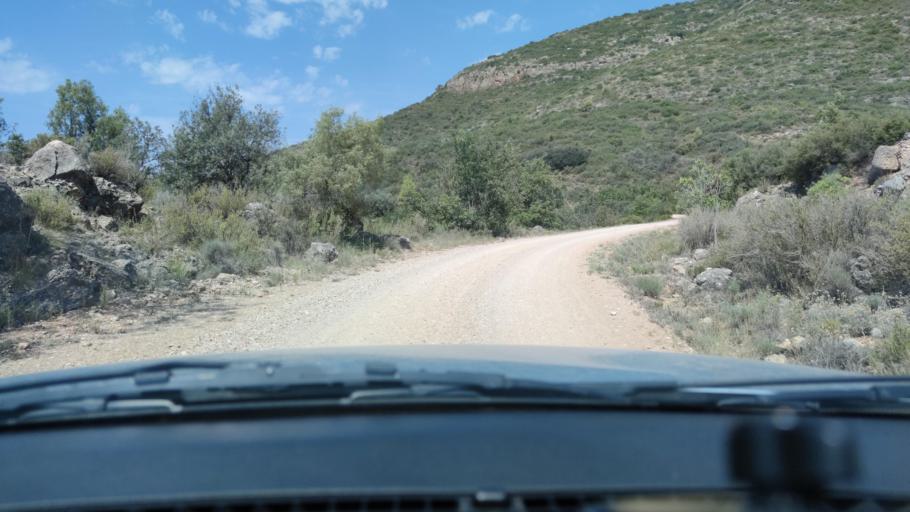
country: ES
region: Catalonia
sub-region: Provincia de Lleida
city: Camarasa
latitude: 41.9261
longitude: 0.8376
